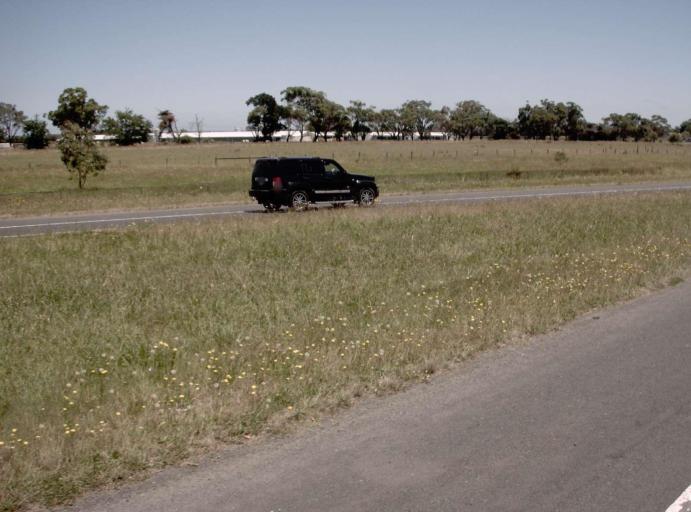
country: AU
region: Victoria
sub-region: Cardinia
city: Pakenham South
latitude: -38.0909
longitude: 145.4681
